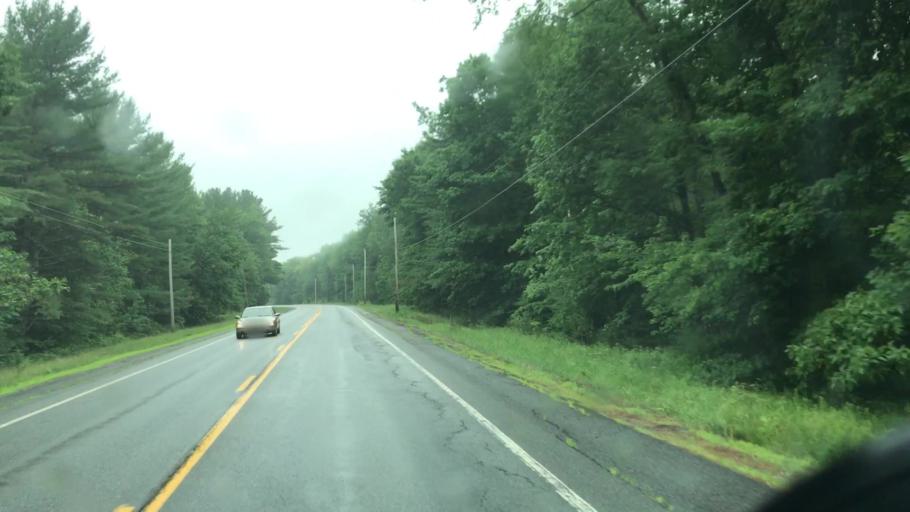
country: US
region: Maine
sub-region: Penobscot County
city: Howland
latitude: 45.2739
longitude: -68.6363
